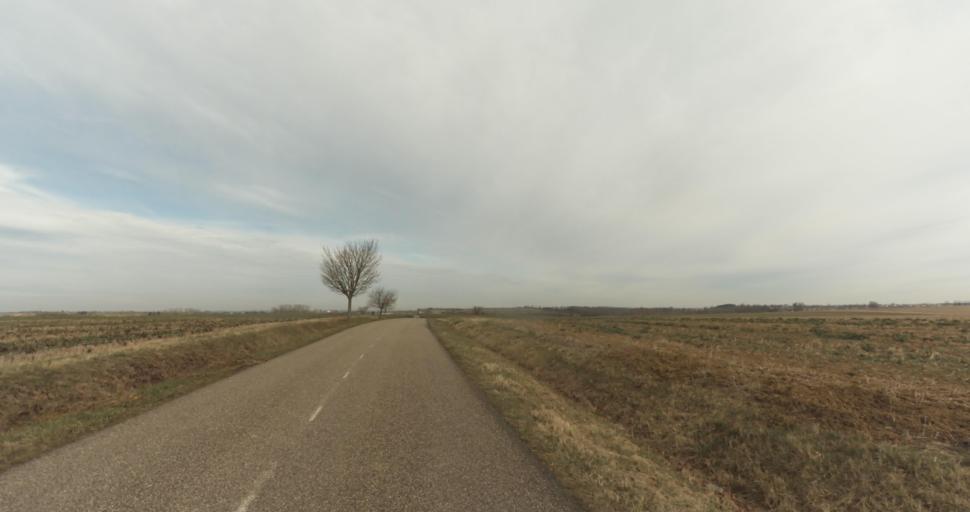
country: FR
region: Lorraine
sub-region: Departement de Meurthe-et-Moselle
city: Conflans-en-Jarnisy
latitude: 49.1364
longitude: 5.8523
